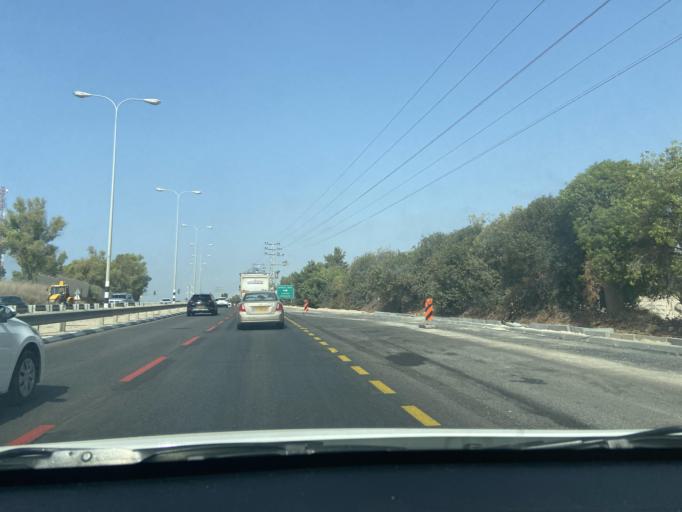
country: IL
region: Northern District
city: El Mazra`a
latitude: 32.9573
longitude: 35.0928
